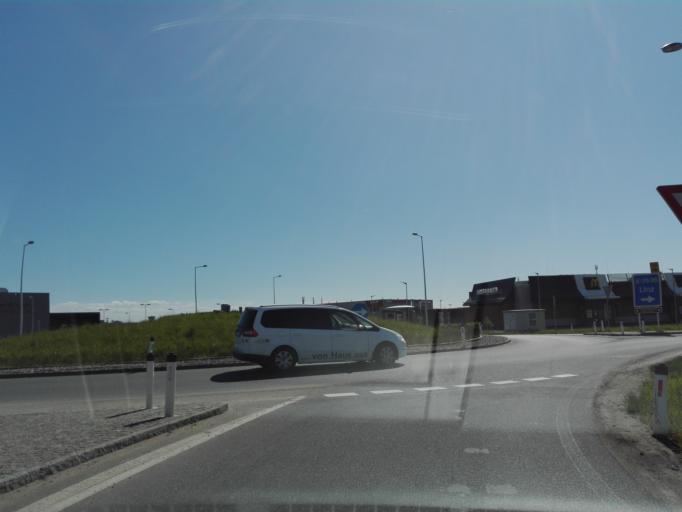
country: AT
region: Upper Austria
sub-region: Politischer Bezirk Urfahr-Umgebung
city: Engerwitzdorf
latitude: 48.3599
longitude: 14.4812
